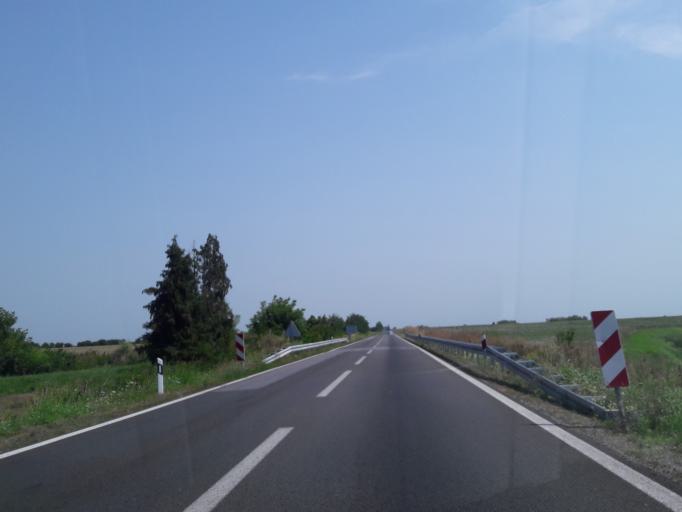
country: HR
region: Osjecko-Baranjska
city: Tenja
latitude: 45.5179
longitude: 18.7831
